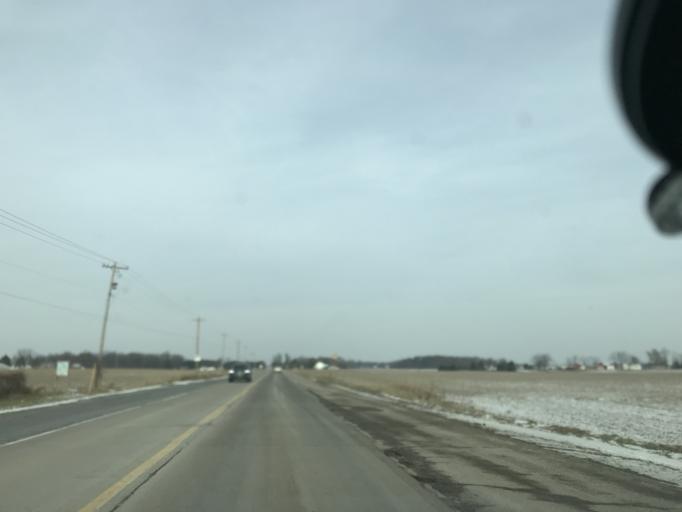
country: US
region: Michigan
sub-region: Ionia County
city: Lake Odessa
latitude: 42.7662
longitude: -85.0743
